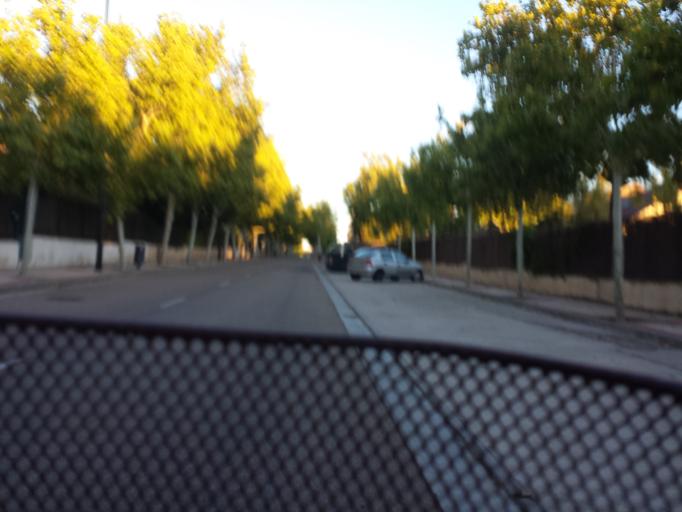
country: ES
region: Aragon
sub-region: Provincia de Zaragoza
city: Montecanal
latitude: 41.6292
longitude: -0.9450
